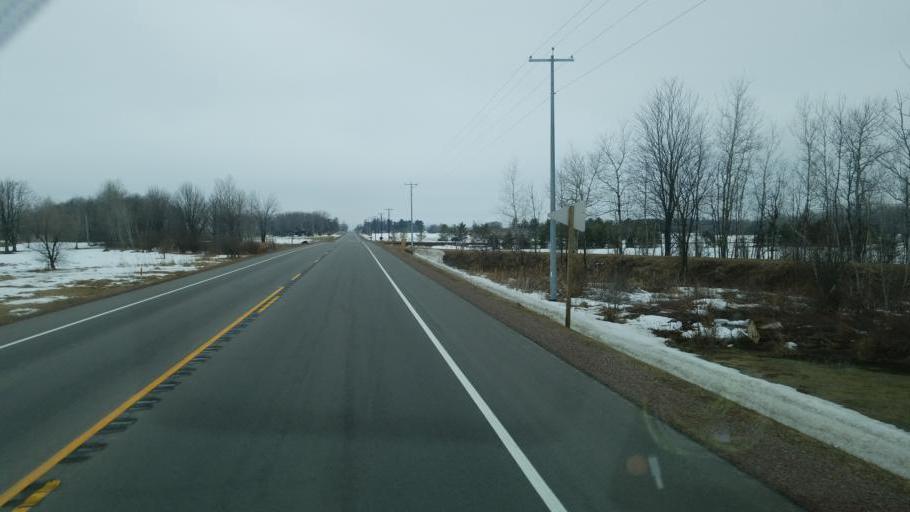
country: US
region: Wisconsin
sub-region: Wood County
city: Marshfield
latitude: 44.6564
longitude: -90.2671
